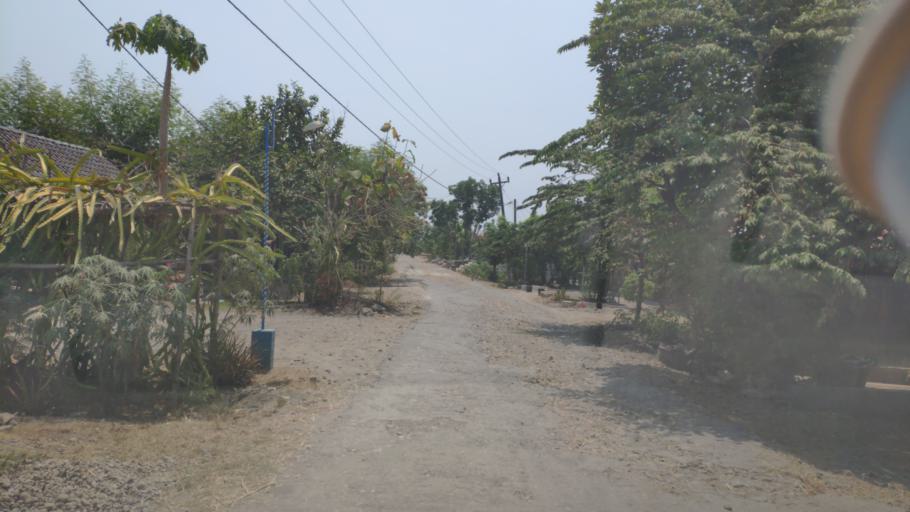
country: ID
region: Central Java
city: Temulus
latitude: -7.2166
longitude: 111.4309
